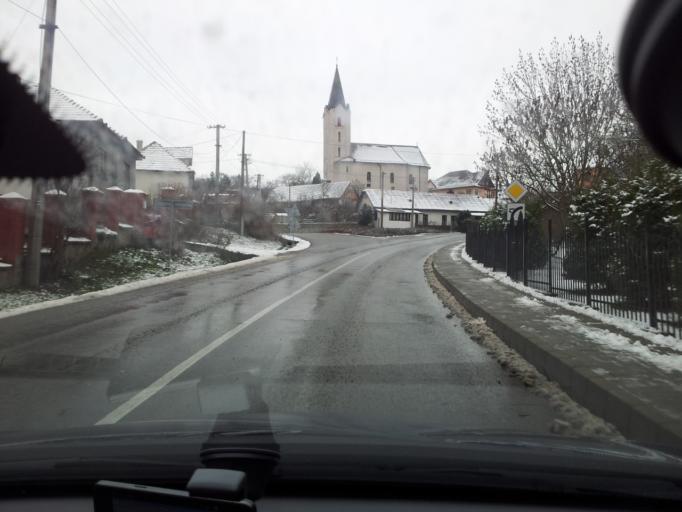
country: SK
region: Presovsky
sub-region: Okres Presov
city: Presov
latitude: 48.8617
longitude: 21.2348
